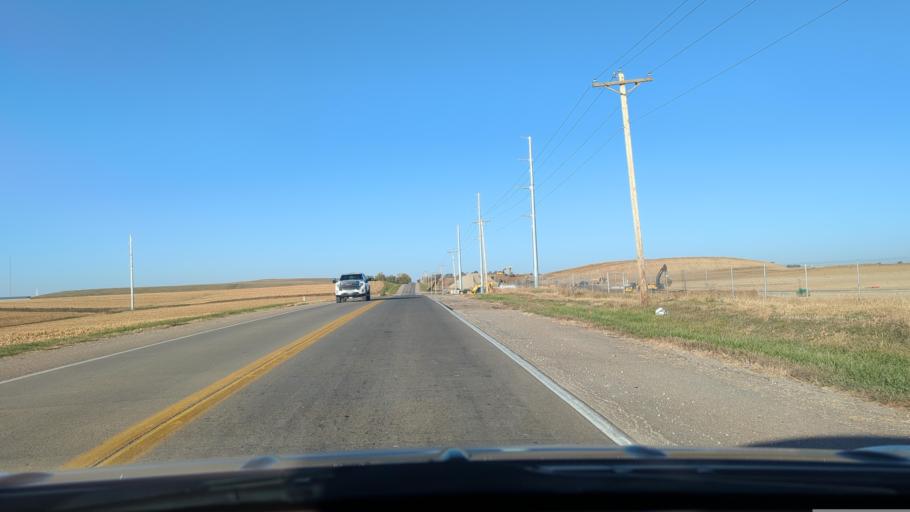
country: US
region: Nebraska
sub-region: Sarpy County
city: Springfield
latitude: 41.1036
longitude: -96.1434
